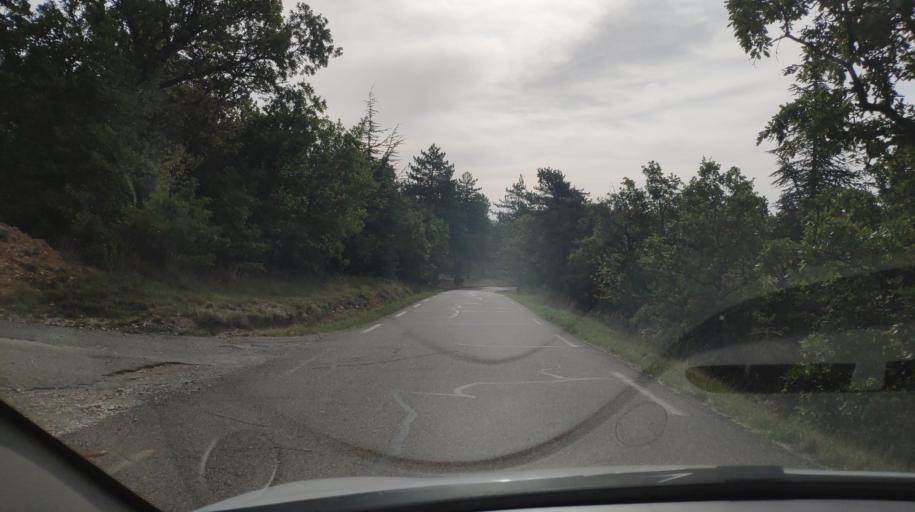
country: FR
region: Provence-Alpes-Cote d'Azur
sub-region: Departement du Vaucluse
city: Sault
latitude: 44.1215
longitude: 5.3771
